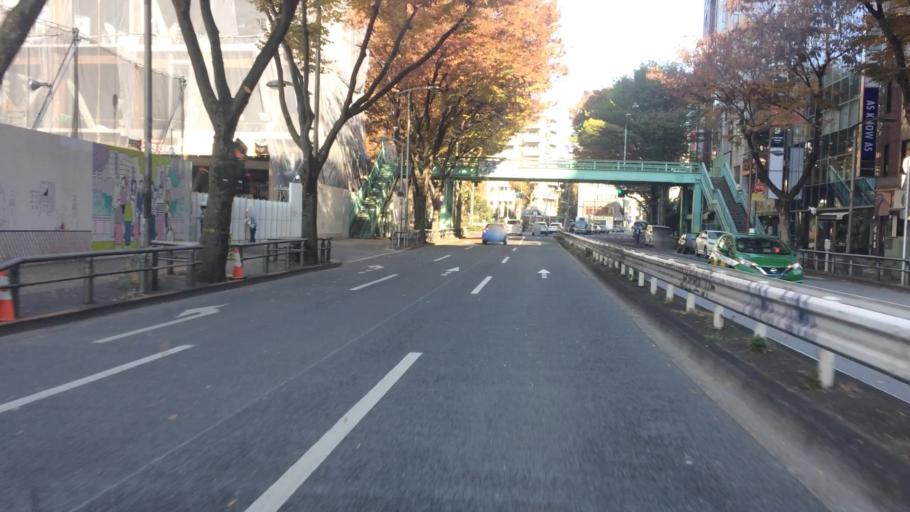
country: JP
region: Tokyo
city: Tokyo
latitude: 35.6626
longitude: 139.7022
